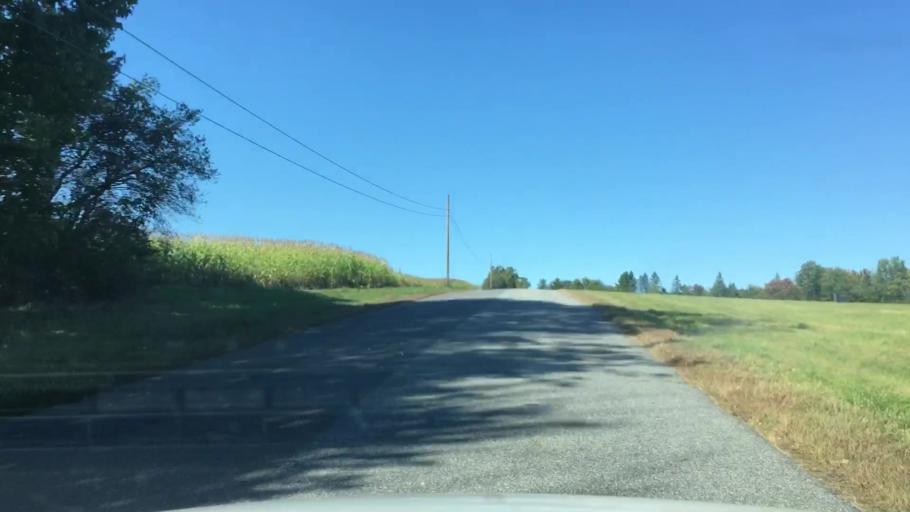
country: US
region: Maine
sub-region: Somerset County
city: Pittsfield
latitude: 44.7862
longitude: -69.4092
